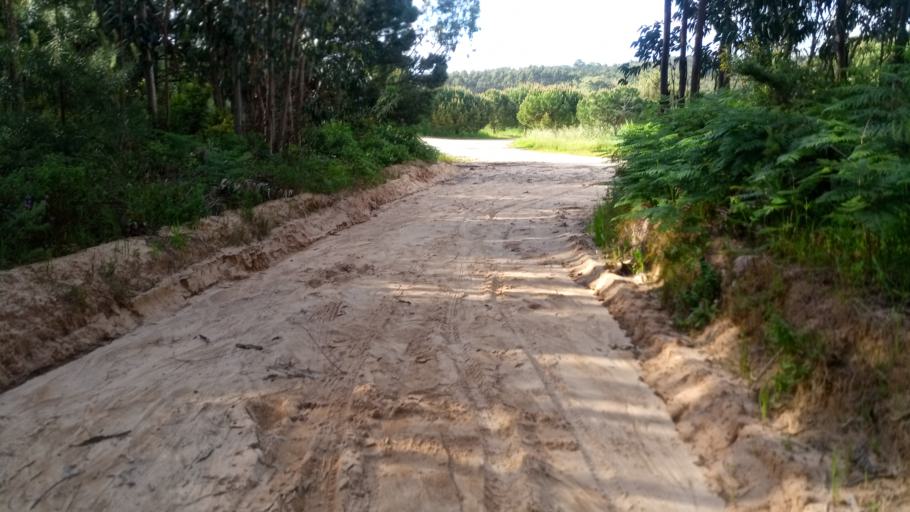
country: PT
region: Leiria
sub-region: Caldas da Rainha
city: Caldas da Rainha
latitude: 39.4022
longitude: -9.1939
